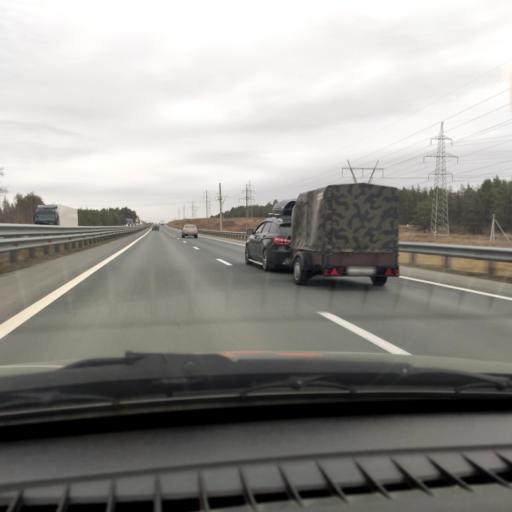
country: RU
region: Samara
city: Povolzhskiy
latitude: 53.5146
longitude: 49.6347
